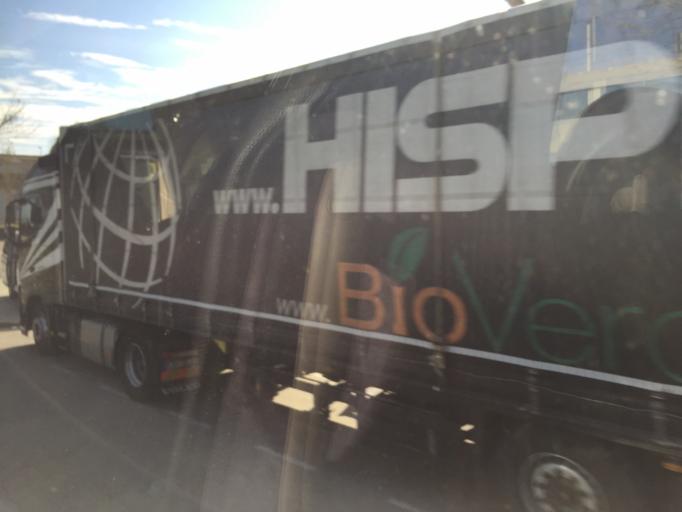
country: ES
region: Catalonia
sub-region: Provincia de Barcelona
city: Sants-Montjuic
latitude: 41.3478
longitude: 2.1336
